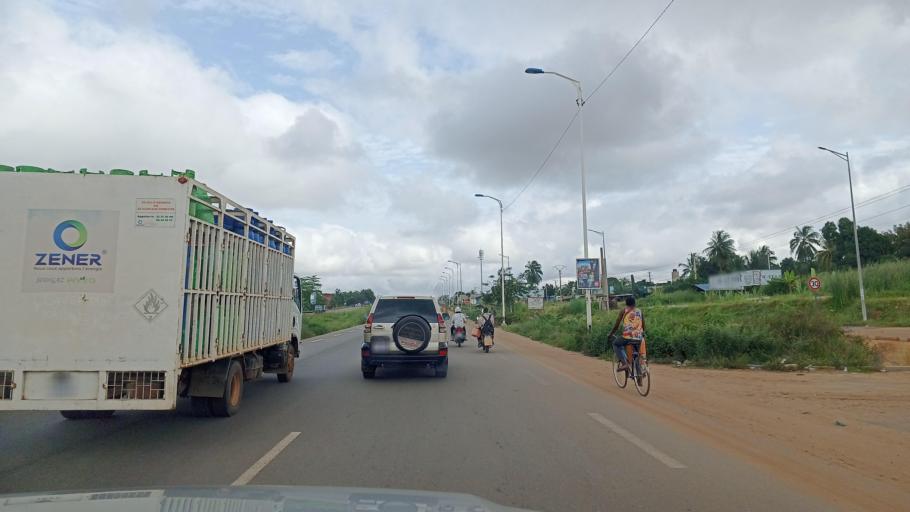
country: TG
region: Maritime
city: Tsevie
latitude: 6.3354
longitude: 1.2167
